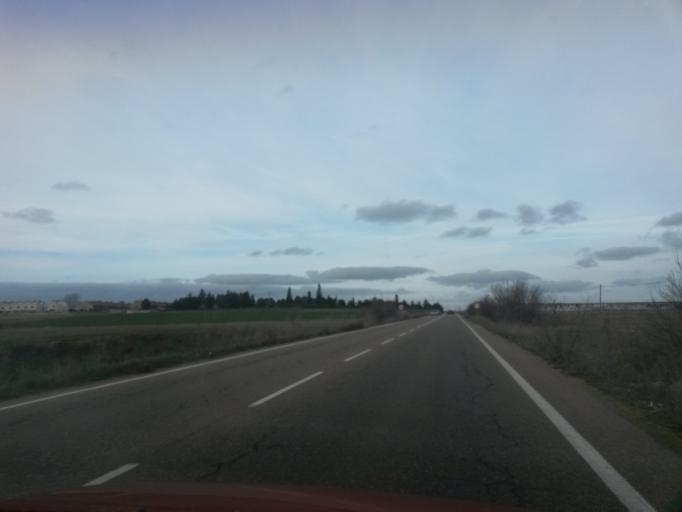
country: ES
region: Castille and Leon
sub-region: Provincia de Salamanca
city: Salamanca
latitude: 40.9884
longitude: -5.6591
